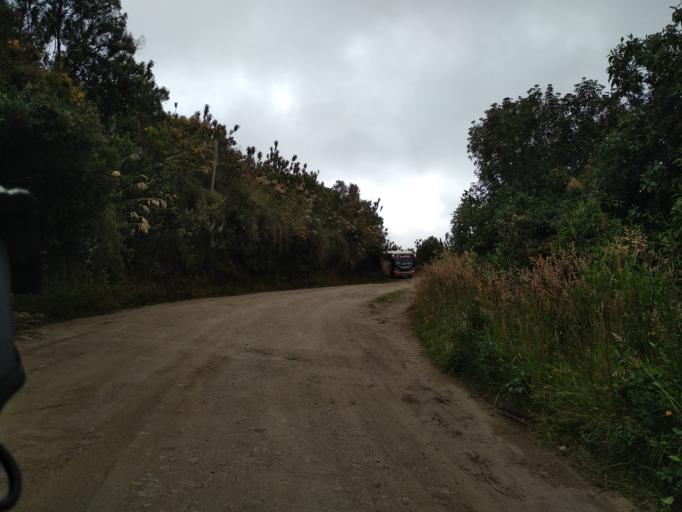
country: EC
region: Carchi
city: Tulcan
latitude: 0.7407
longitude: -77.7883
